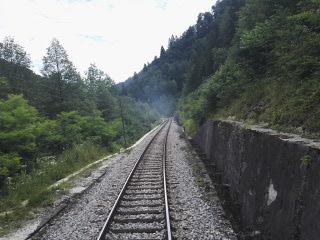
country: SI
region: Cerkno
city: Cerkno
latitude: 46.1725
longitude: 13.9124
